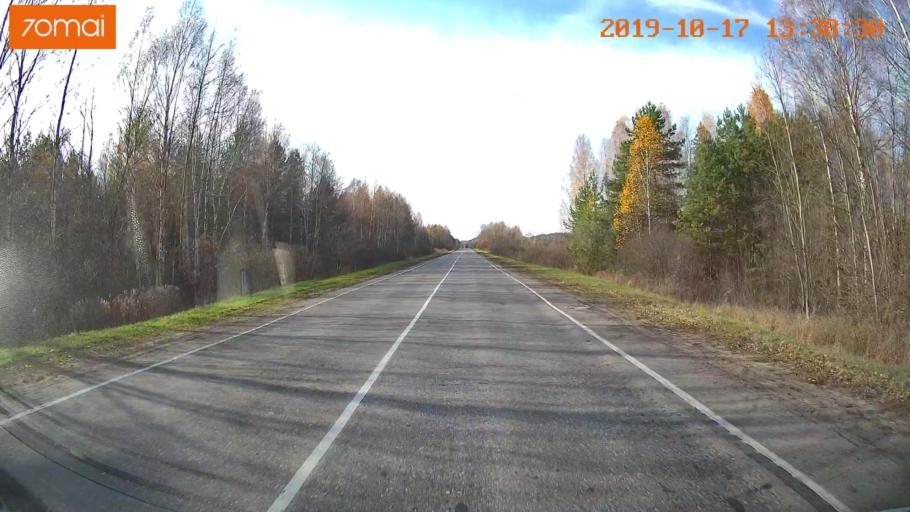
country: RU
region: Rjazan
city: Tuma
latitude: 55.1440
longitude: 40.6120
